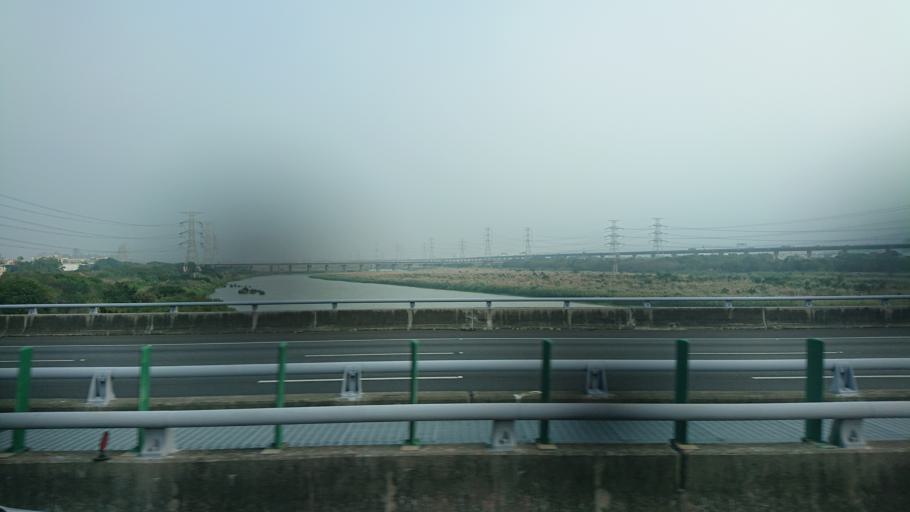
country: TW
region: Taiwan
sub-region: Changhua
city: Chang-hua
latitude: 24.1124
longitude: 120.5673
